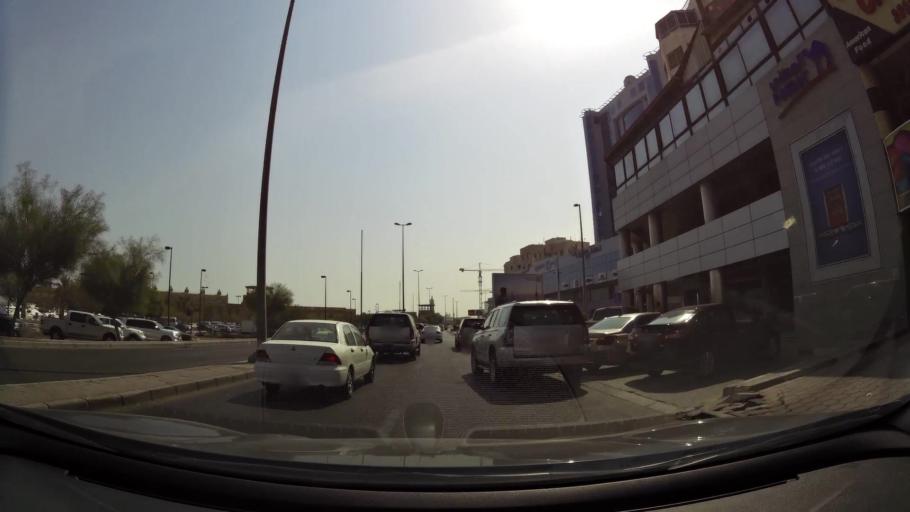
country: KW
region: Al Ahmadi
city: Al Fahahil
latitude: 29.0828
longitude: 48.1398
